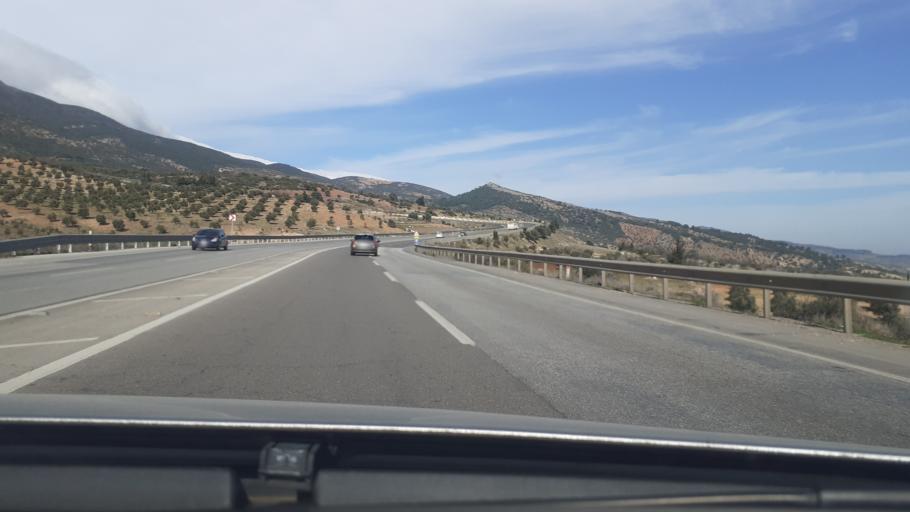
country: TR
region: Hatay
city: Kirikhan
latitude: 36.4822
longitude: 36.2778
